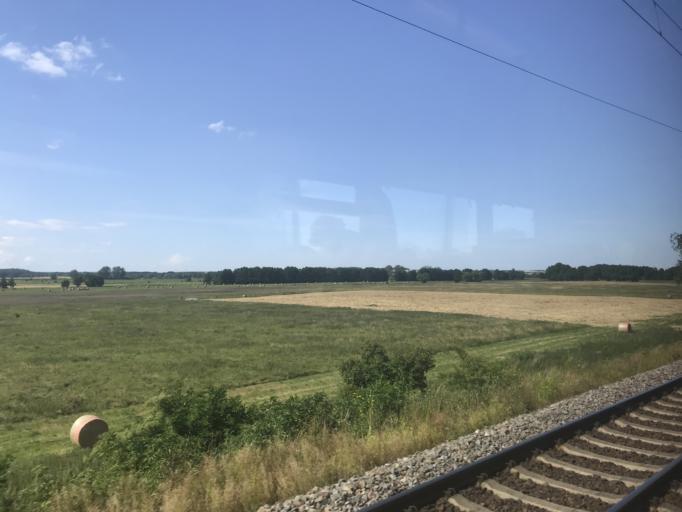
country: DE
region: Brandenburg
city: Pinnow
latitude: 53.0977
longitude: 14.0220
